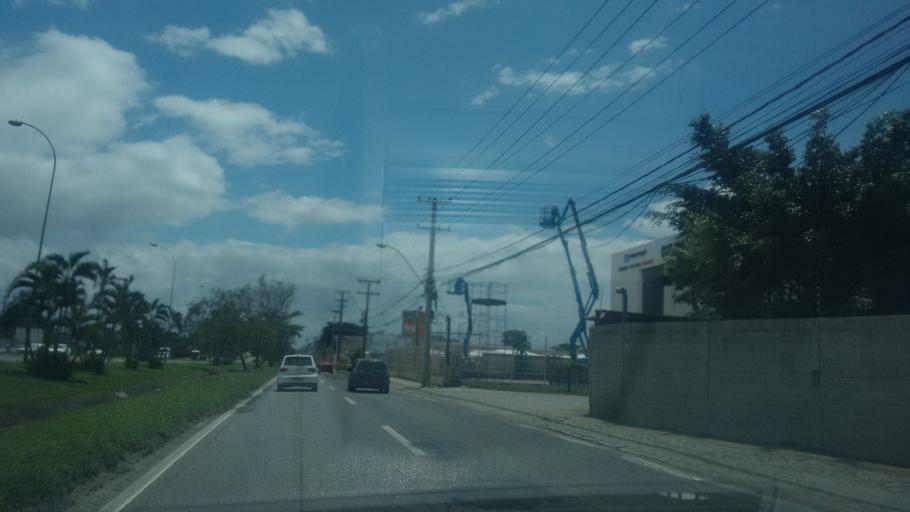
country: BR
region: Espirito Santo
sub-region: Serra
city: Serra
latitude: -20.2034
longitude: -40.2690
